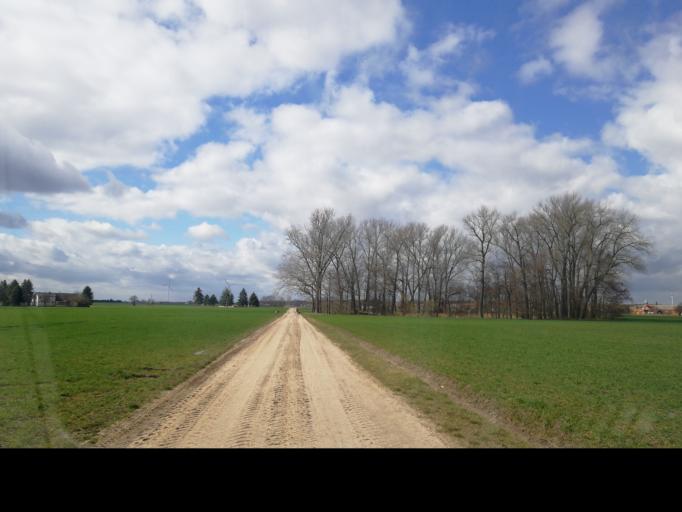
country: DE
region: Brandenburg
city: Schonewalde
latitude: 51.6865
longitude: 13.5441
